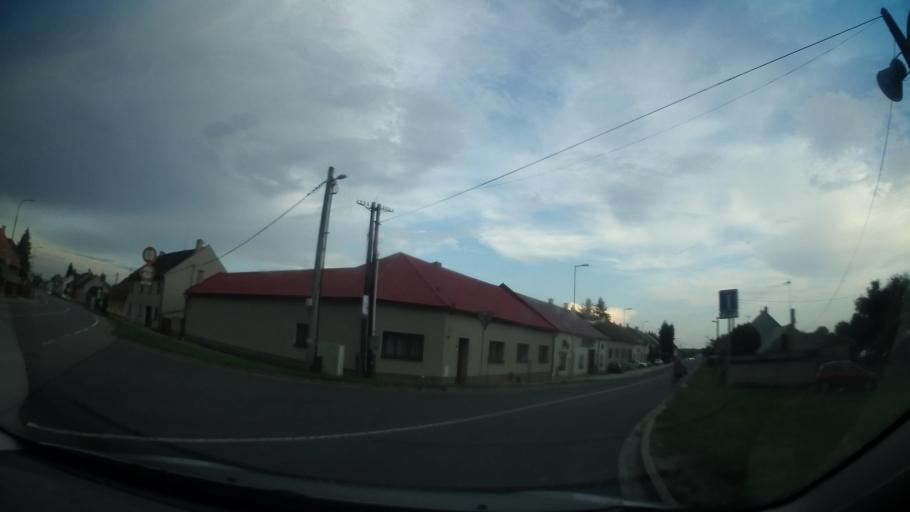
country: CZ
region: Olomoucky
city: Troubky
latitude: 49.4300
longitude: 17.3390
